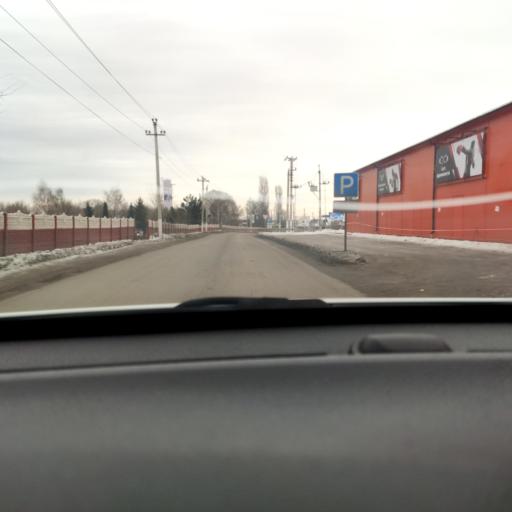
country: RU
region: Voronezj
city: Novaya Usman'
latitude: 51.6698
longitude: 39.3370
